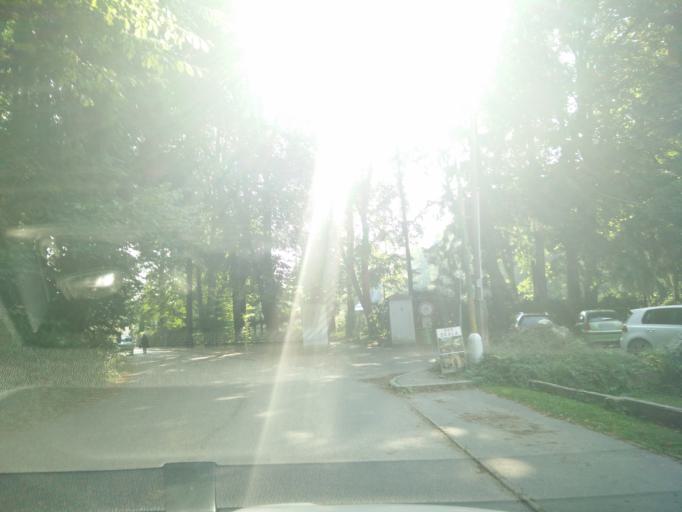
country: SK
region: Zilinsky
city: Rajec
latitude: 49.1313
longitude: 18.6852
